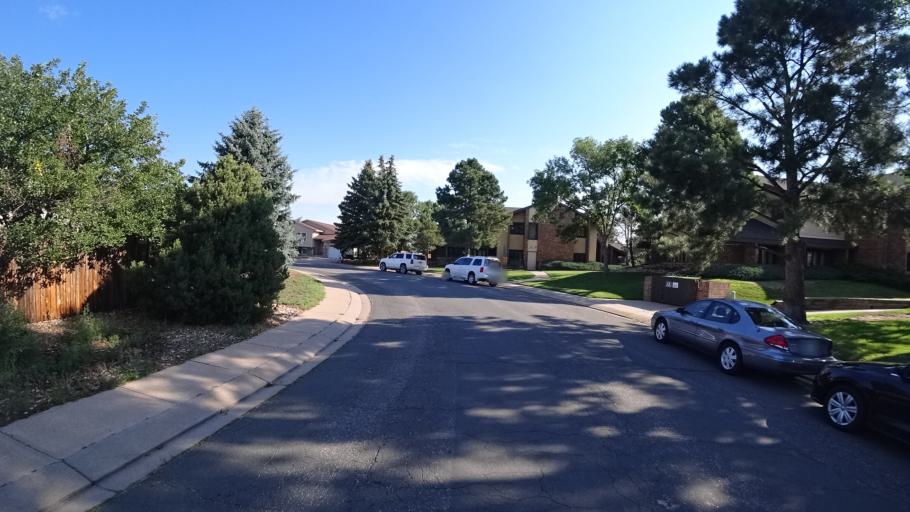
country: US
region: Colorado
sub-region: El Paso County
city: Black Forest
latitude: 38.9450
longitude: -104.7752
